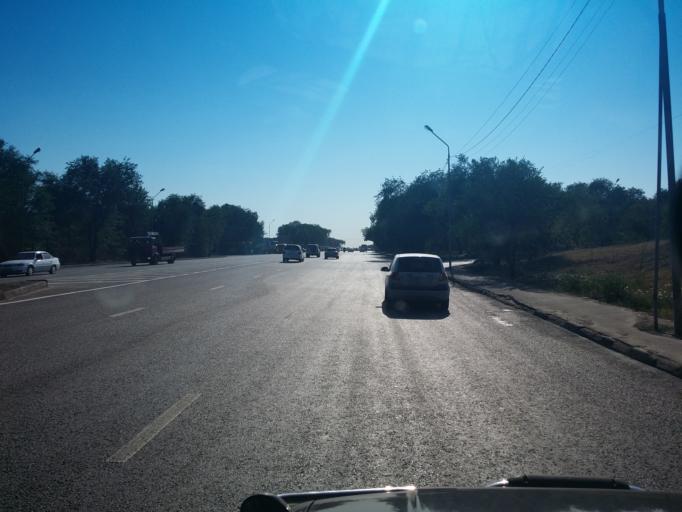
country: KZ
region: Almaty Oblysy
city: Pervomayskiy
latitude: 43.3538
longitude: 76.9383
